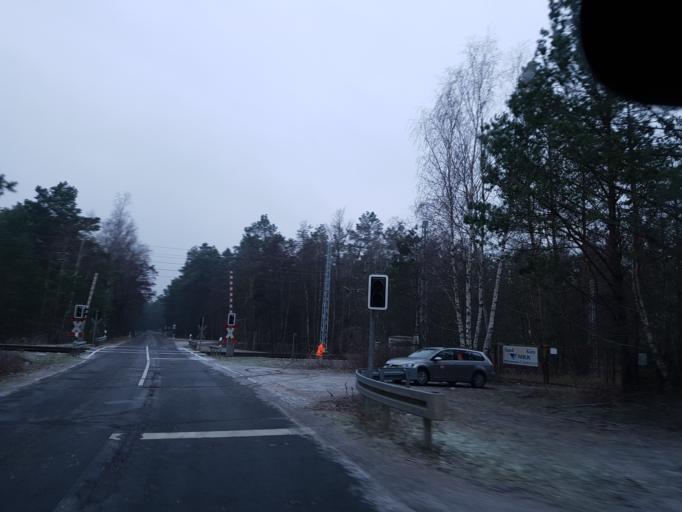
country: DE
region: Brandenburg
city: Finsterwalde
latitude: 51.6285
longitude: 13.6463
